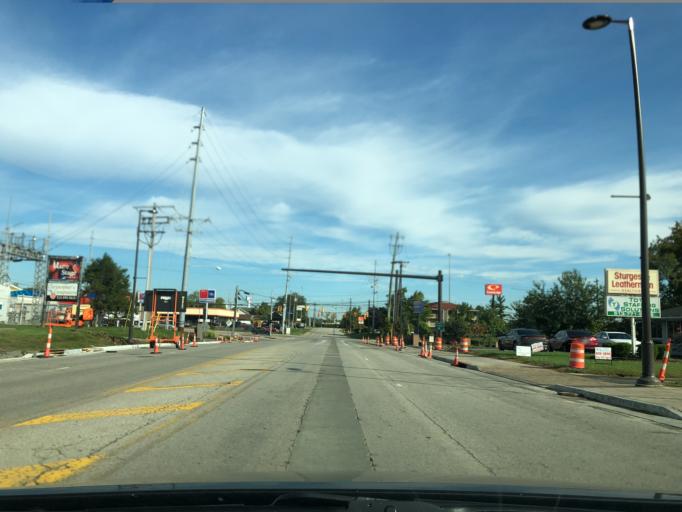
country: US
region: Ohio
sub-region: Hamilton County
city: Glendale
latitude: 39.2840
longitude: -84.4431
